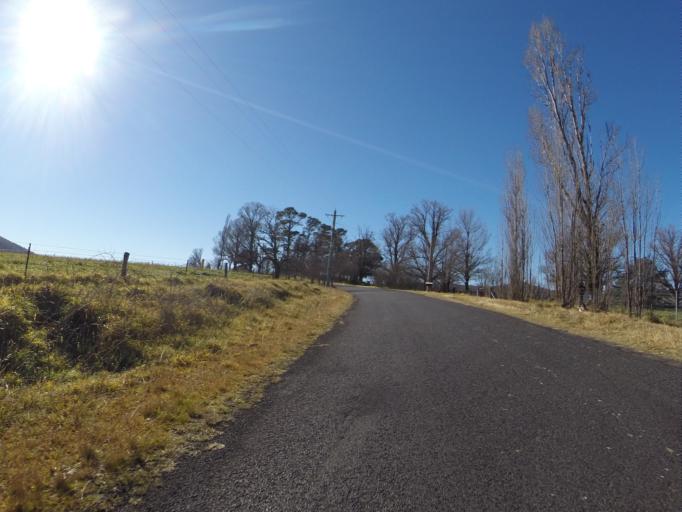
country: AU
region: New South Wales
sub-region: Oberon
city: Oberon
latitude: -33.5390
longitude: 149.8838
